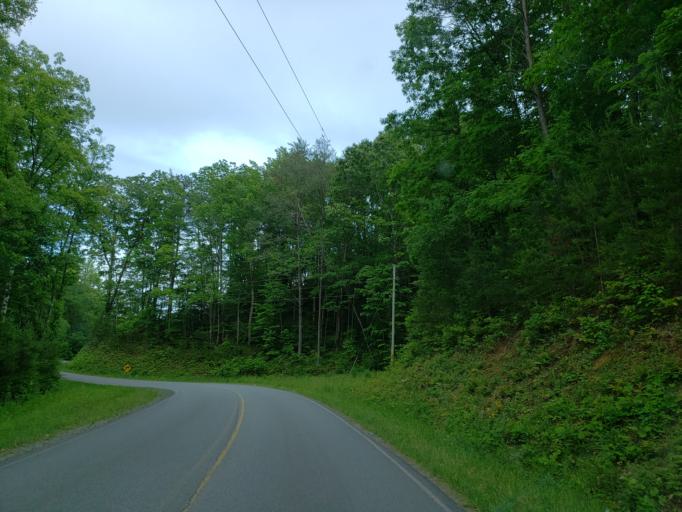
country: US
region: Georgia
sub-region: Fannin County
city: Blue Ridge
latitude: 34.8645
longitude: -84.3539
